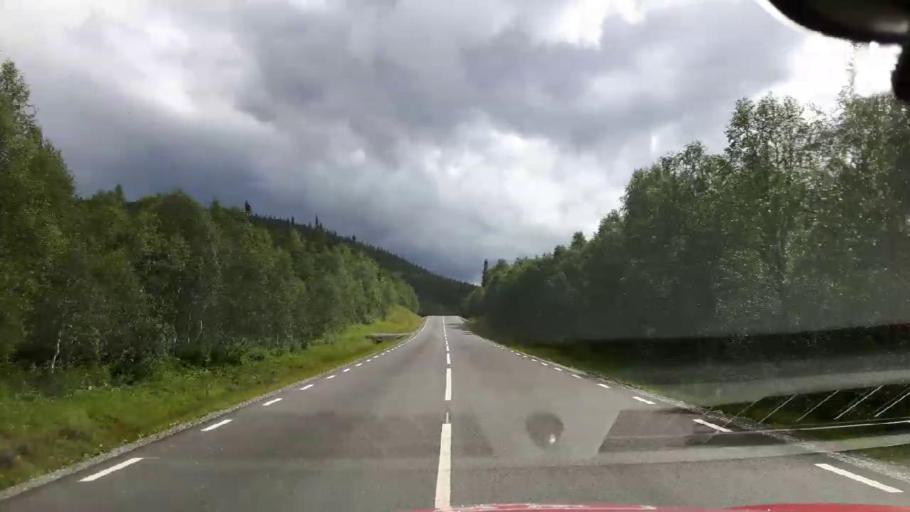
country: NO
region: Nord-Trondelag
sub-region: Royrvik
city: Royrvik
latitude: 64.8877
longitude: 14.1939
